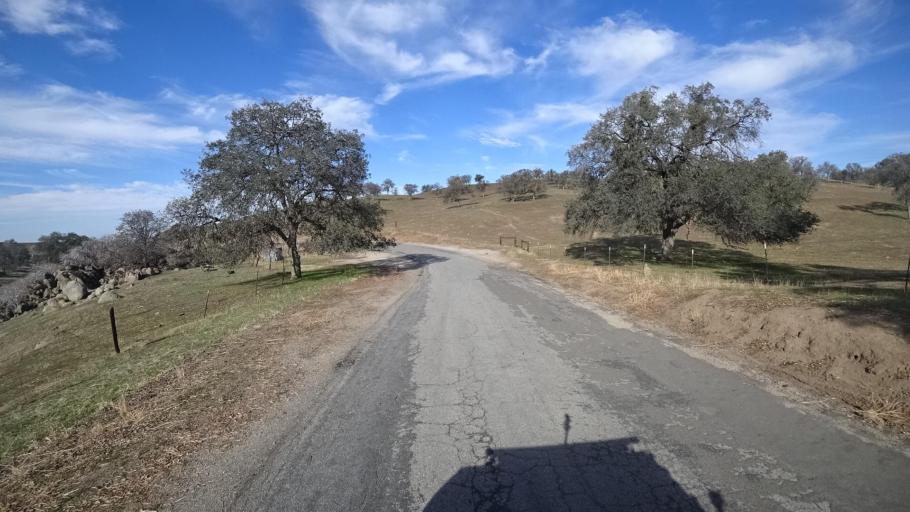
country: US
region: California
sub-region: Kern County
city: Oildale
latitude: 35.6147
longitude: -118.8428
